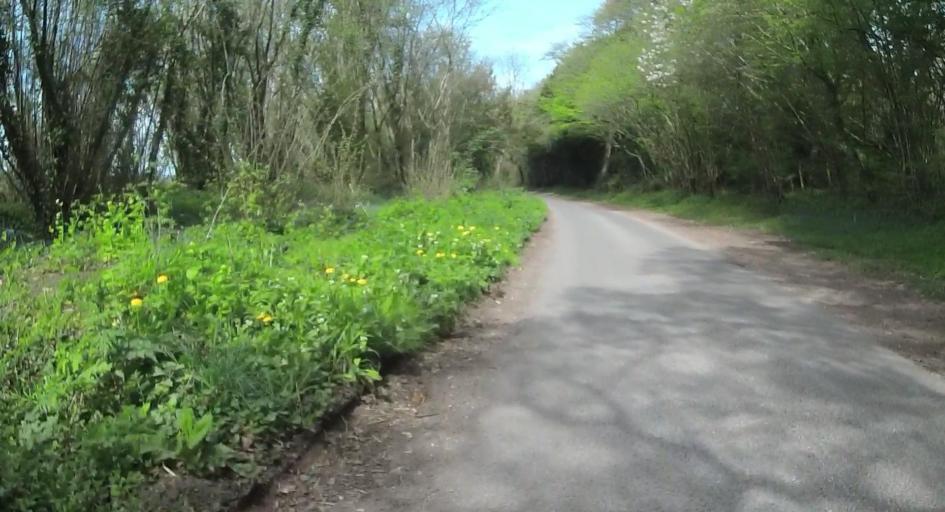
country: GB
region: England
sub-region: Hampshire
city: Chandlers Ford
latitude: 51.0731
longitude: -1.4505
